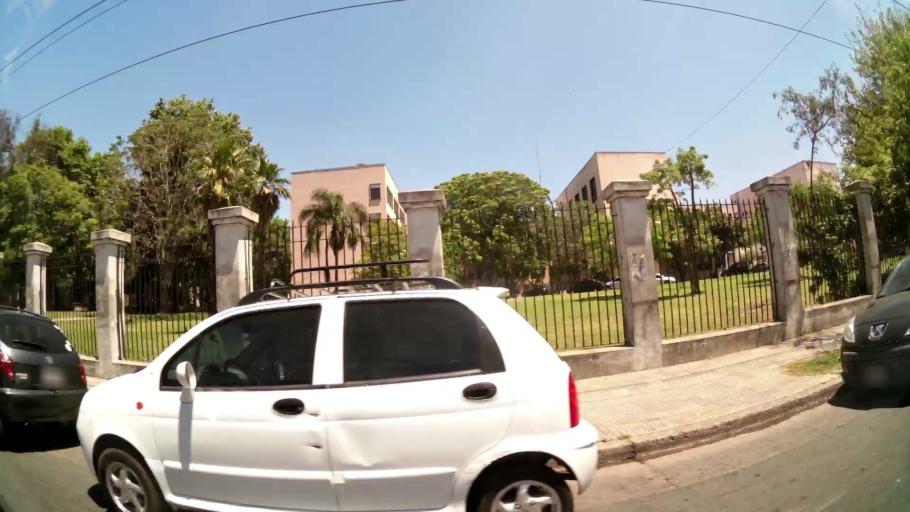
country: AR
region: Buenos Aires F.D.
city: Buenos Aires
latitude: -34.6373
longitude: -58.3817
